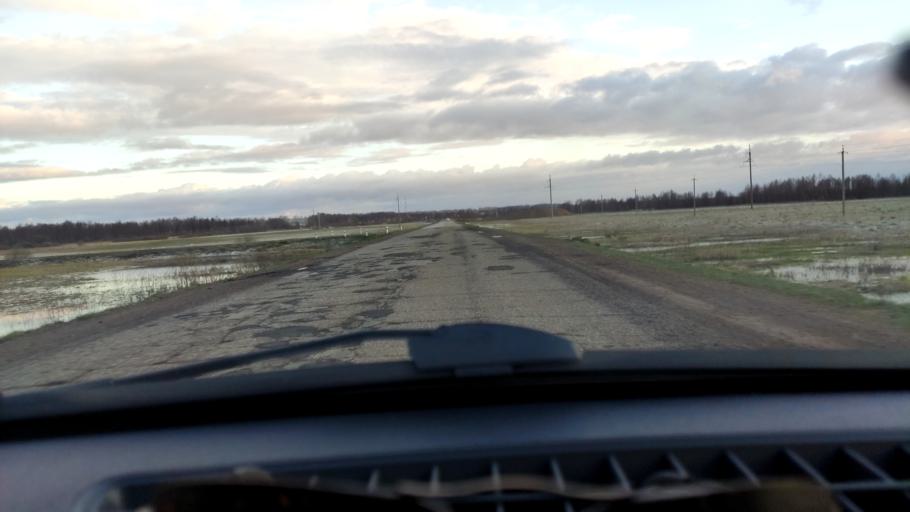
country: RU
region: Bashkortostan
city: Kabakovo
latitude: 54.5013
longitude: 56.1762
